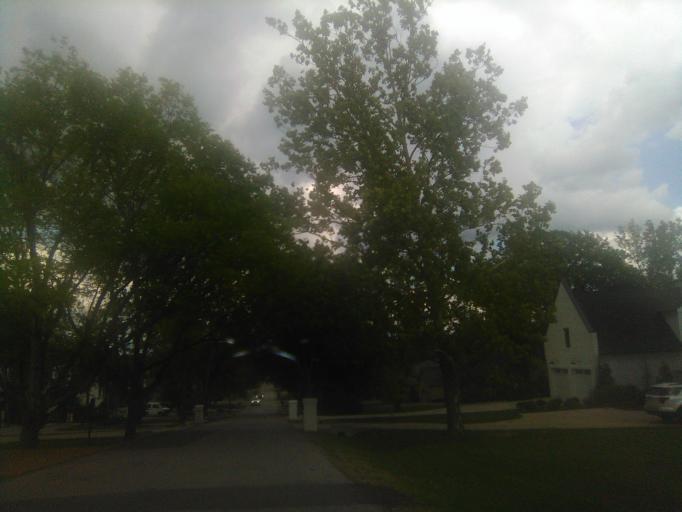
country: US
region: Tennessee
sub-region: Davidson County
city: Belle Meade
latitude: 36.1002
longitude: -86.8276
